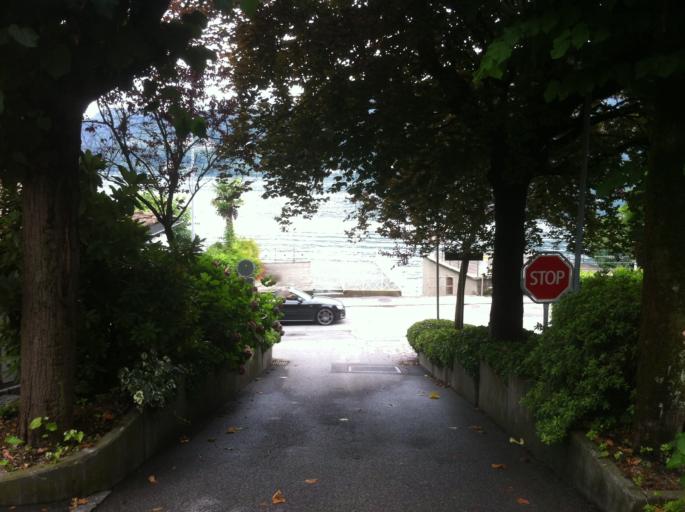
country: IT
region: Lombardy
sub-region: Provincia di Varese
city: Porto Ceresio
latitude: 45.9274
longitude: 8.9073
